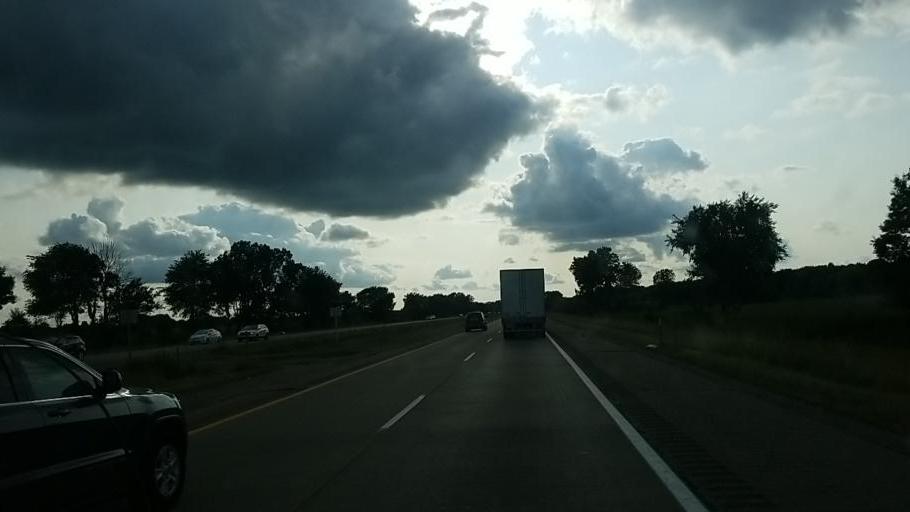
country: US
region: Michigan
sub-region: Kent County
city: Lowell
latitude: 42.8751
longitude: -85.3279
